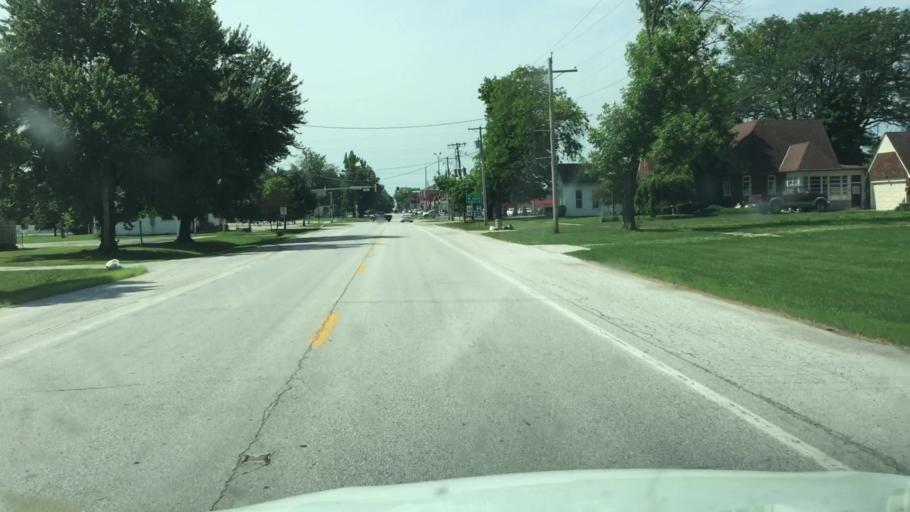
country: US
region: Illinois
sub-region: Hancock County
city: Carthage
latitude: 40.4179
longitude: -91.1362
